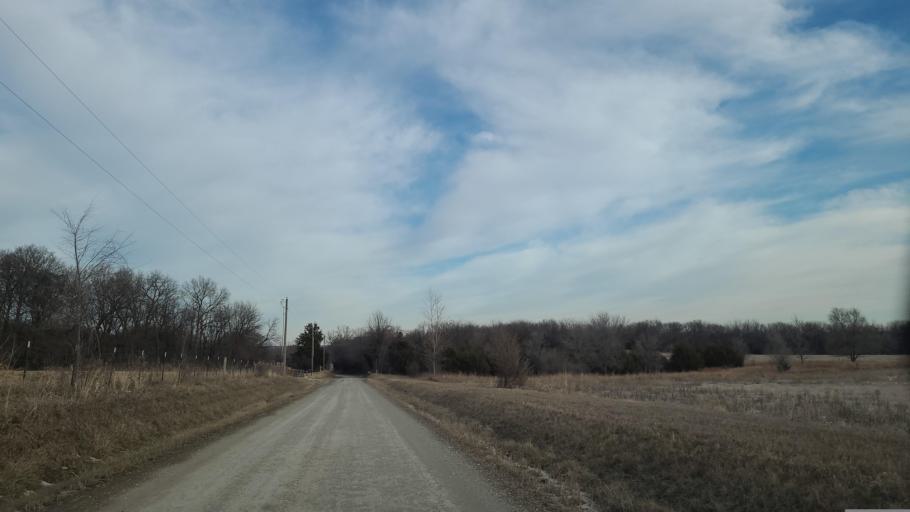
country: US
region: Kansas
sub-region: Jefferson County
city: Oskaloosa
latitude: 39.0530
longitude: -95.4097
